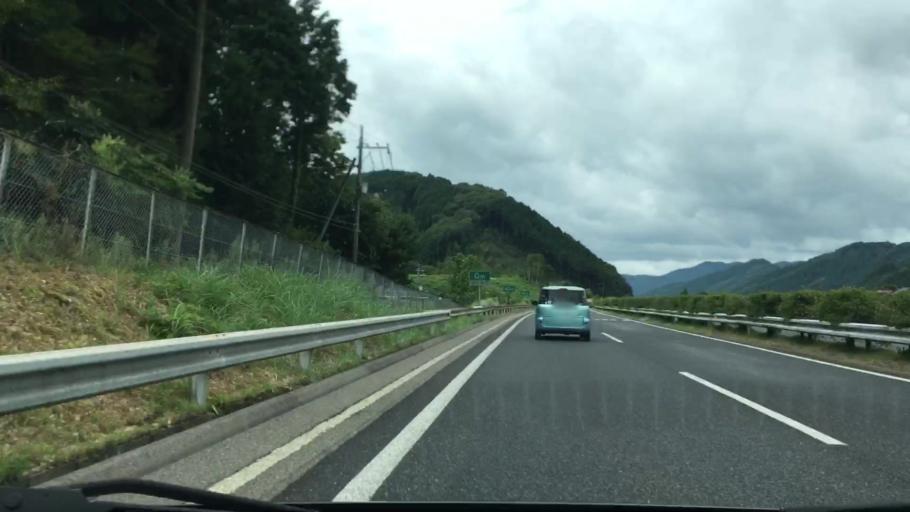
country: JP
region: Okayama
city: Tsuyama
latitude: 35.0344
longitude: 133.7871
